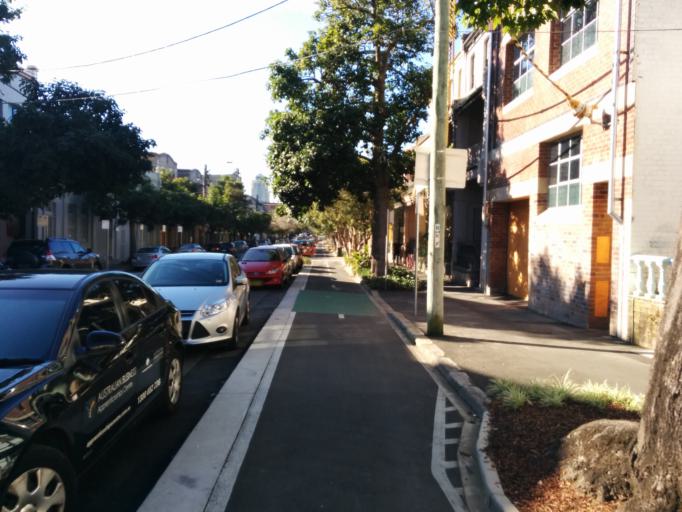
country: AU
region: New South Wales
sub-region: City of Sydney
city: Redfern
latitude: -33.8918
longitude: 151.2024
